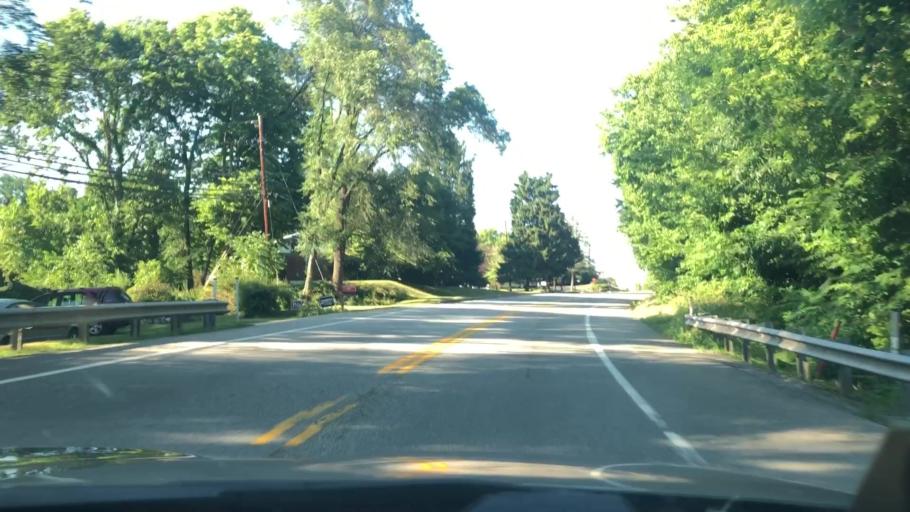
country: US
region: Pennsylvania
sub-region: Cumberland County
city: Mechanicsburg
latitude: 40.2435
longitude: -77.0081
